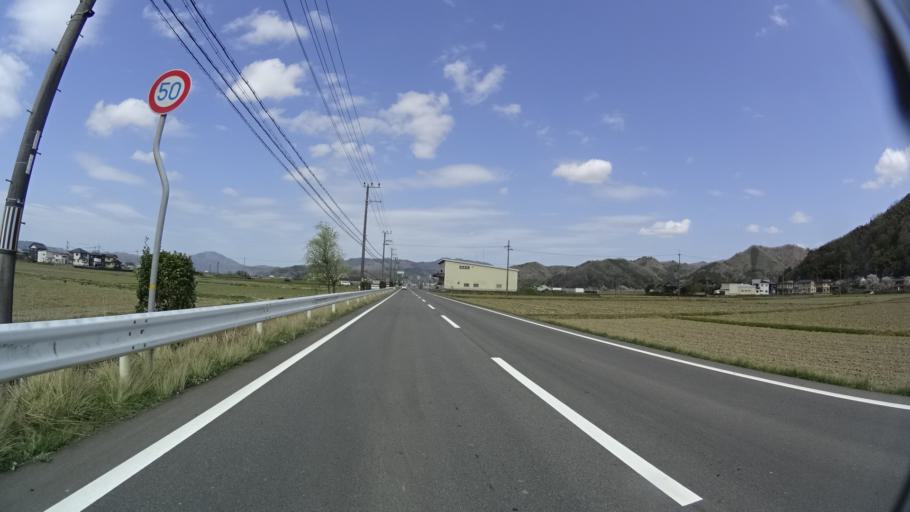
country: JP
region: Hyogo
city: Toyooka
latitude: 35.5225
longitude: 134.8399
